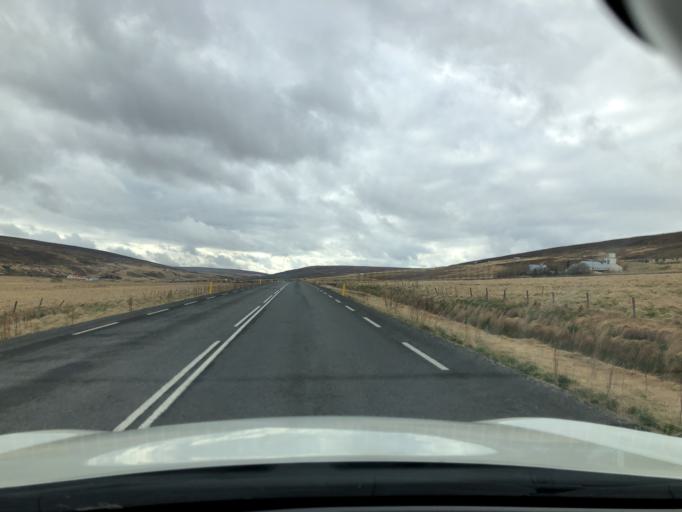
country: IS
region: Northeast
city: Laugar
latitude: 65.7098
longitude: -17.3633
